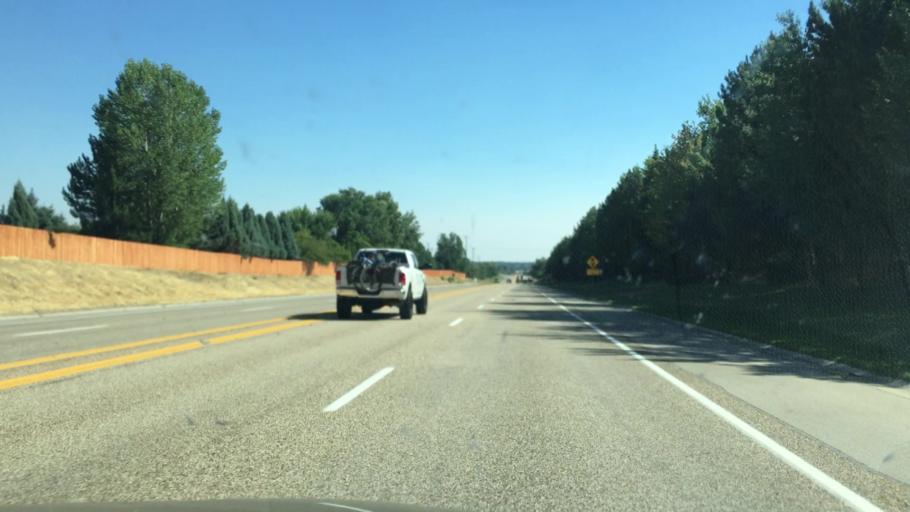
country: US
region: Idaho
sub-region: Ada County
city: Eagle
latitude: 43.7104
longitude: -116.3189
